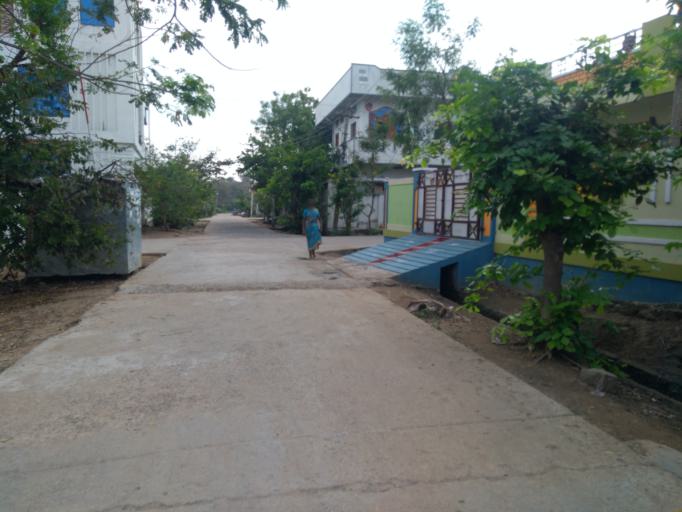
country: IN
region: Telangana
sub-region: Warangal
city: Warangal
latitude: 17.9522
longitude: 79.6019
